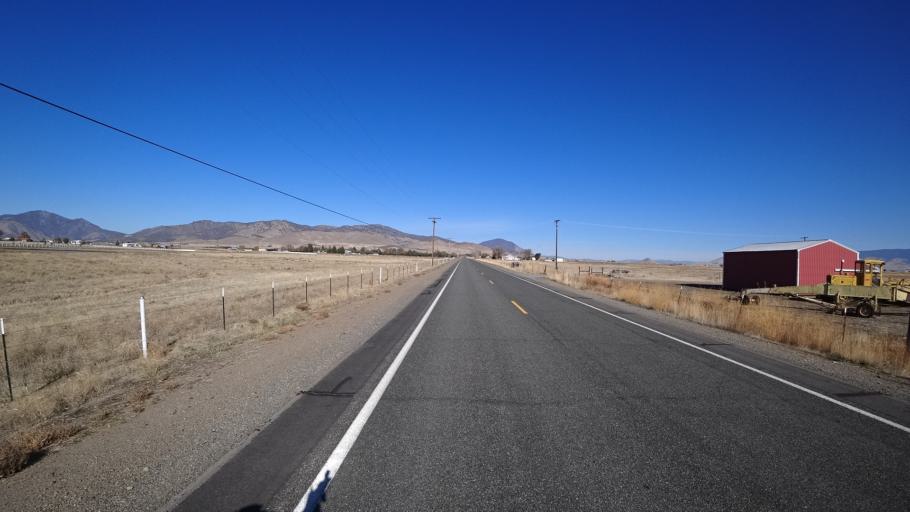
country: US
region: California
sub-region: Siskiyou County
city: Montague
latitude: 41.7468
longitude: -122.5247
